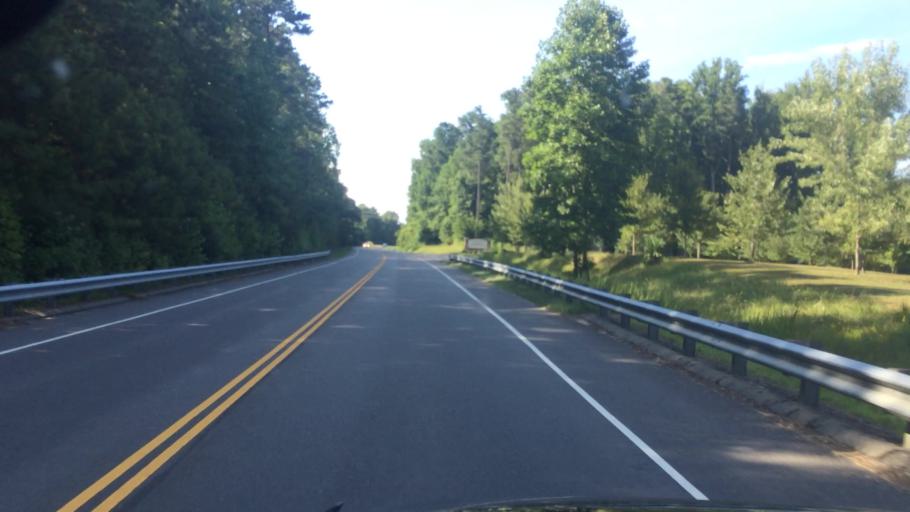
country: US
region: Virginia
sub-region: James City County
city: Williamsburg
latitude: 37.2988
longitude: -76.7252
